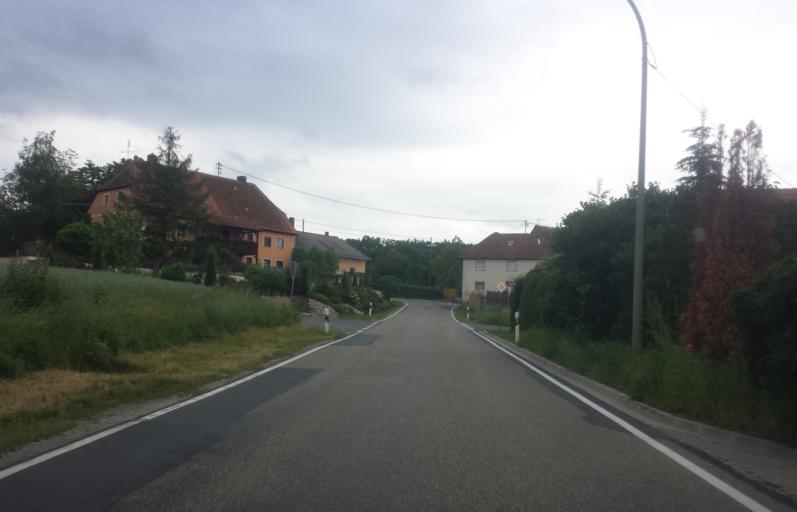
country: DE
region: Bavaria
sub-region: Regierungsbezirk Mittelfranken
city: Munchsteinach
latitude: 49.6652
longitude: 10.5781
